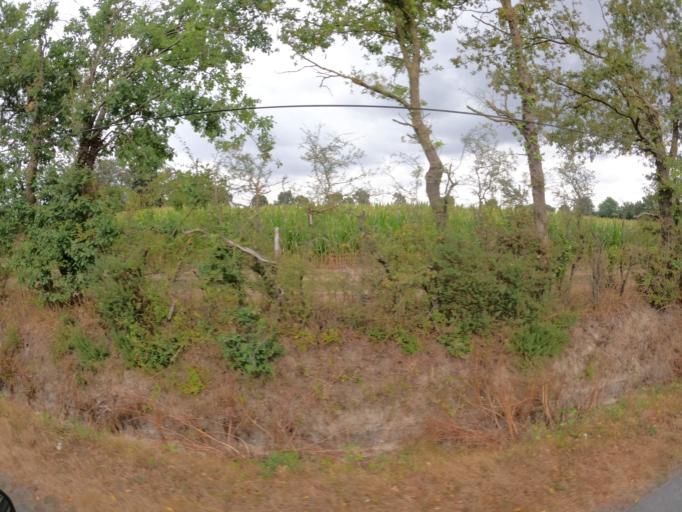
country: FR
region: Pays de la Loire
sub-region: Departement de la Vendee
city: Tiffauges
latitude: 46.9981
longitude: -1.0931
